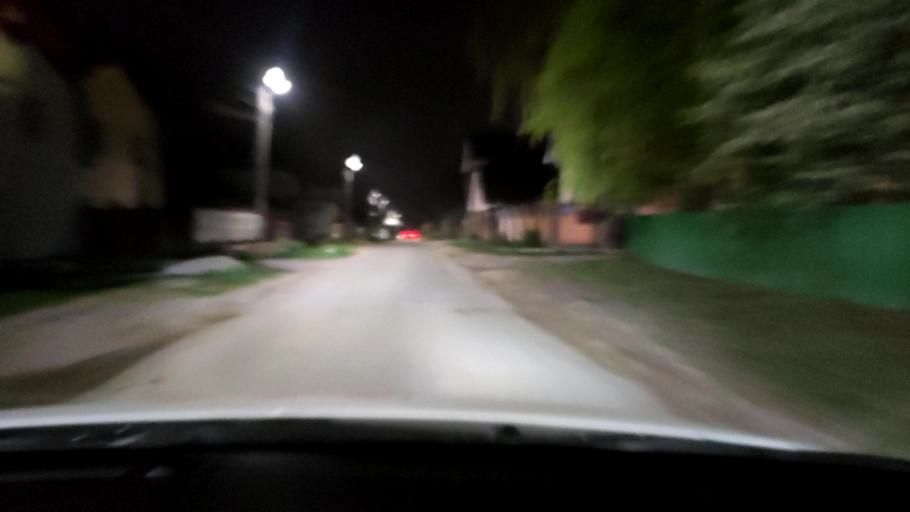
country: RU
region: Tatarstan
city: Stolbishchi
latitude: 55.7040
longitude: 49.1500
